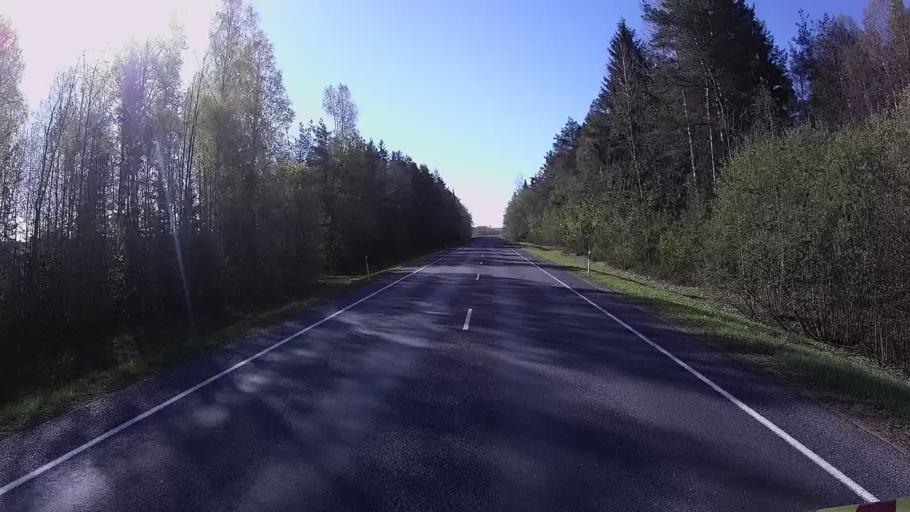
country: EE
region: Viljandimaa
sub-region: Vohma linn
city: Vohma
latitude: 58.7420
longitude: 25.5802
